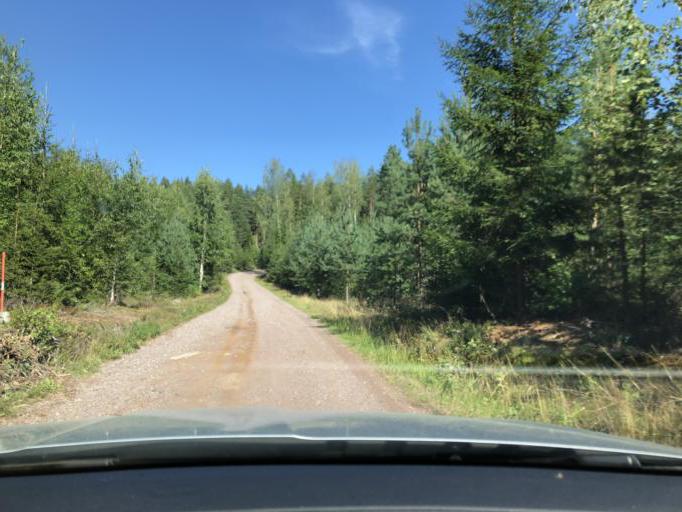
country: SE
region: Dalarna
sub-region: Hedemora Kommun
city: Hedemora
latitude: 60.3252
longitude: 15.8964
